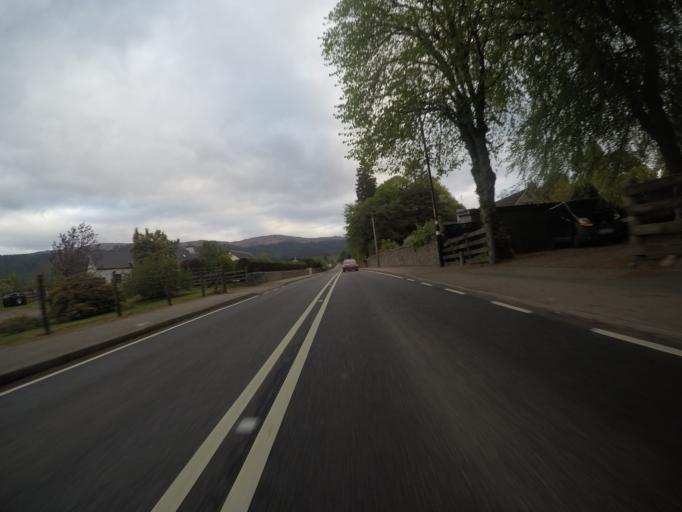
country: GB
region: Scotland
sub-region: Highland
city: Spean Bridge
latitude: 57.1383
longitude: -4.6881
